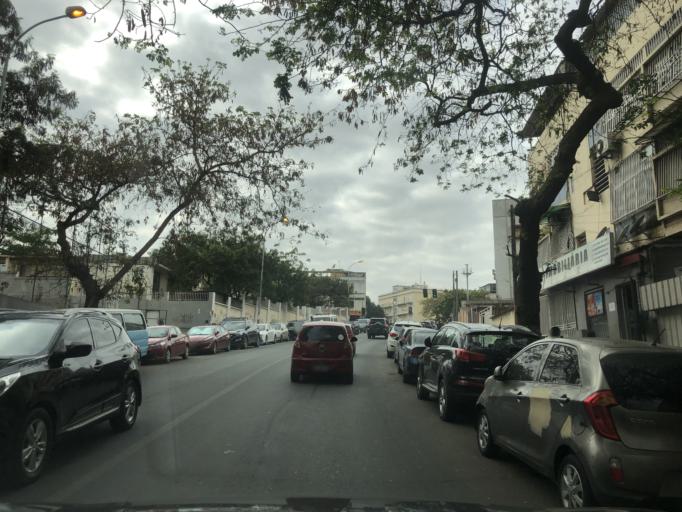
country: AO
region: Luanda
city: Luanda
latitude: -8.8249
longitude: 13.2335
